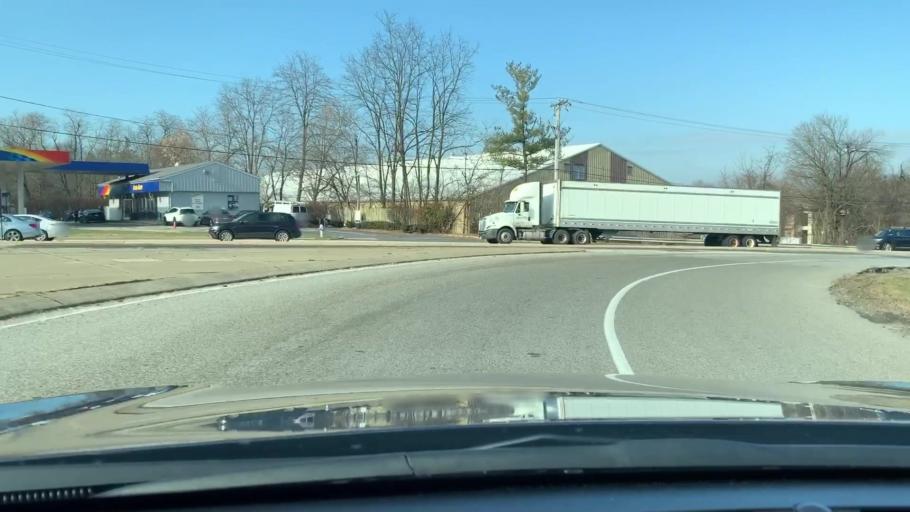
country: US
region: Pennsylvania
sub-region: Chester County
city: Malvern
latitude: 40.0441
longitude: -75.5233
